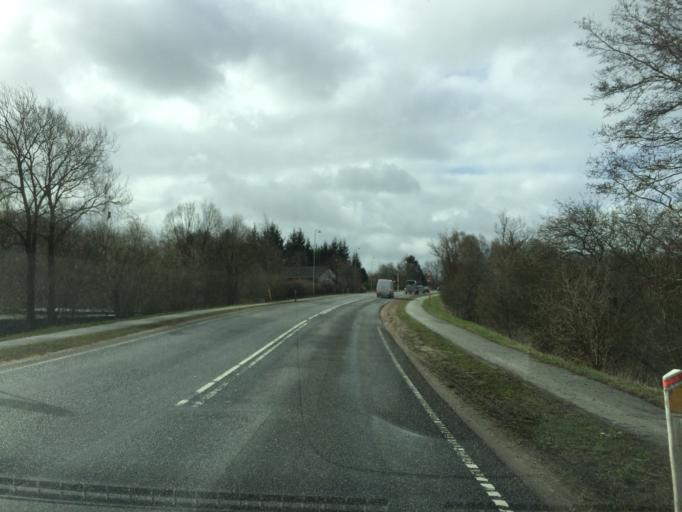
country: DK
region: Central Jutland
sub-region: Silkeborg Kommune
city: Silkeborg
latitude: 56.1542
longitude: 9.4982
